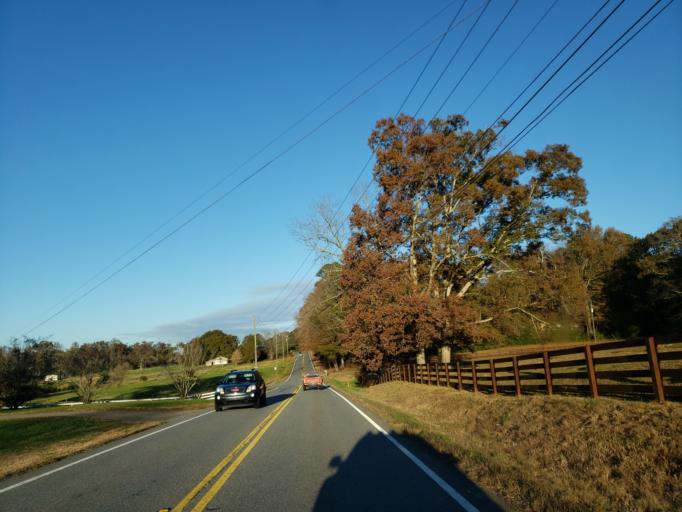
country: US
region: Georgia
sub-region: Cherokee County
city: Canton
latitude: 34.2018
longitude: -84.4147
